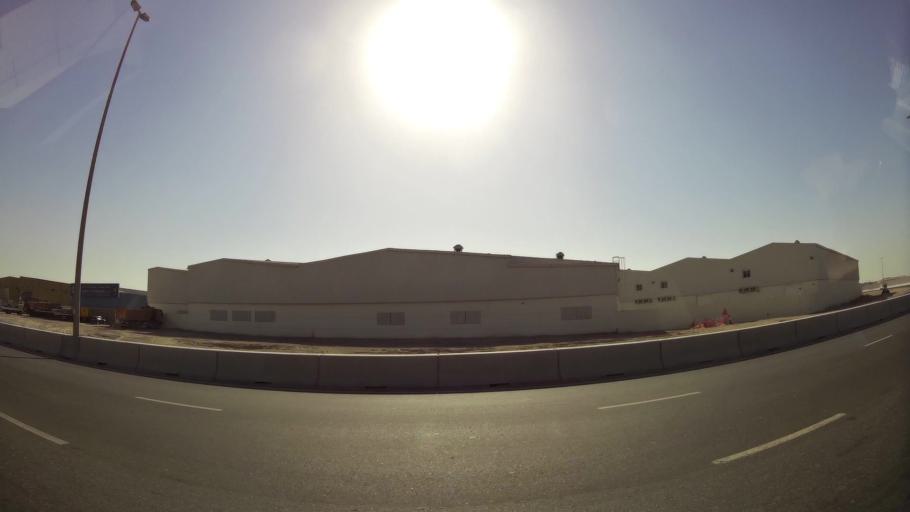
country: AE
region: Dubai
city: Dubai
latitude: 24.9857
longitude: 55.1166
